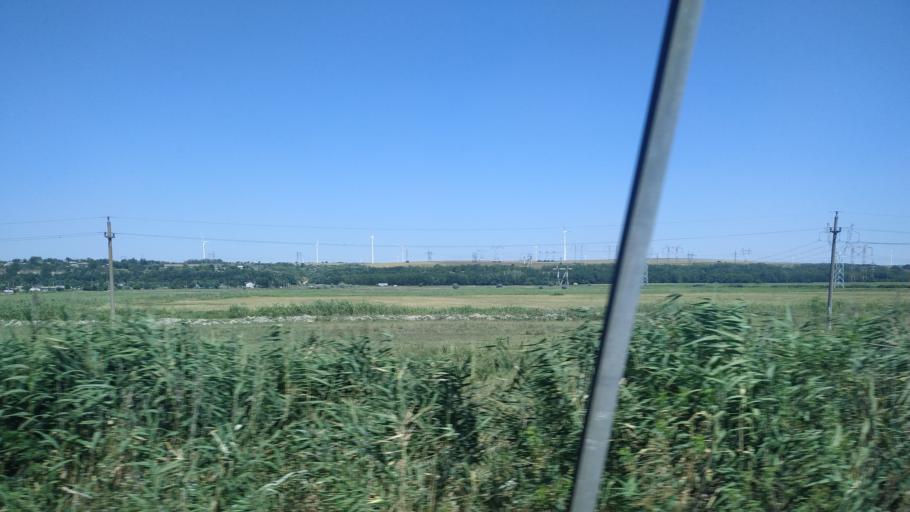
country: RO
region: Constanta
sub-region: Comuna Saligny
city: Faclia
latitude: 44.2705
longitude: 28.1167
